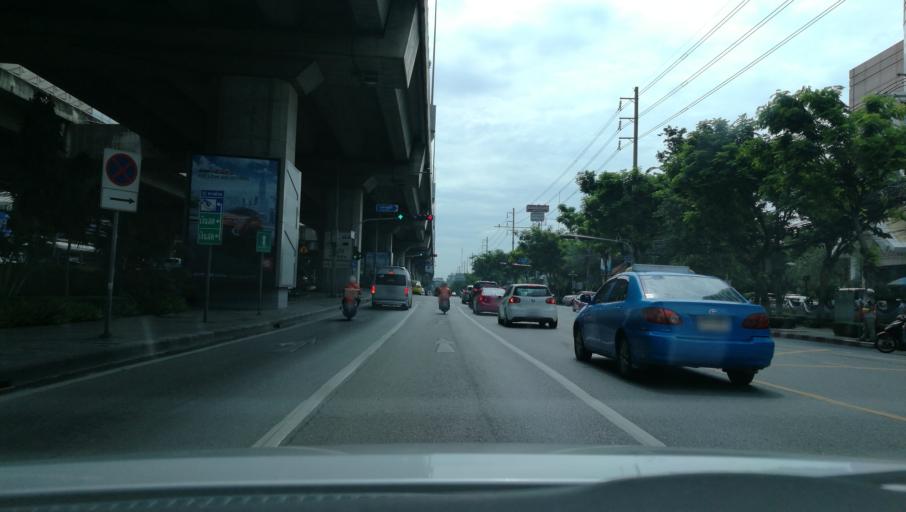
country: TH
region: Bangkok
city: Phaya Thai
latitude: 13.7809
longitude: 100.5335
